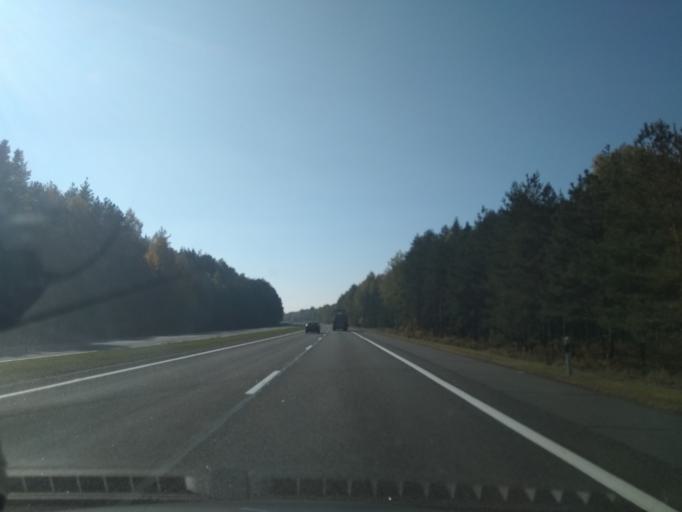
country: BY
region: Brest
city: Ivatsevichy
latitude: 52.8280
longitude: 25.5959
